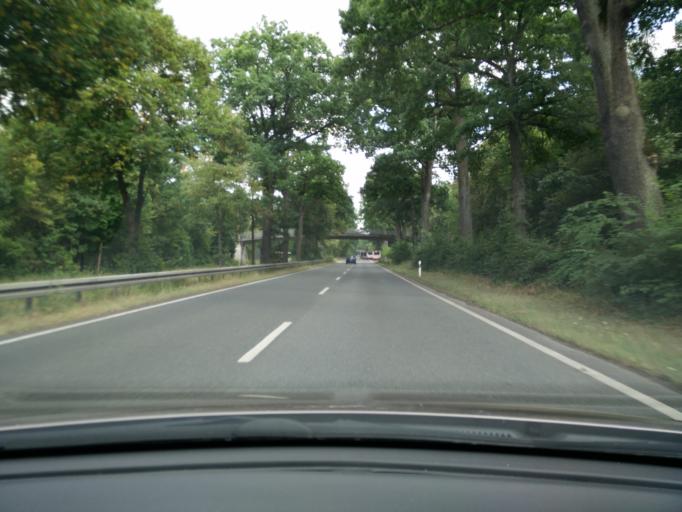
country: DE
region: Bavaria
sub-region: Regierungsbezirk Mittelfranken
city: Erlangen
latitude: 49.5735
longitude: 11.0213
